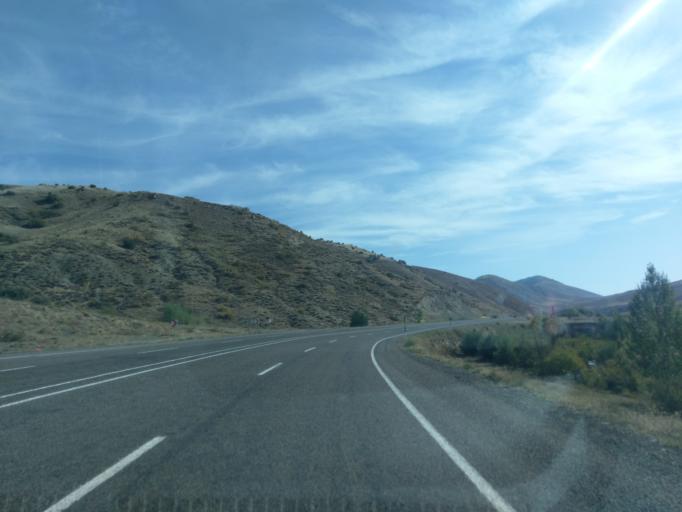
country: TR
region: Sivas
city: Imranli
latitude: 39.8627
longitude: 38.3303
